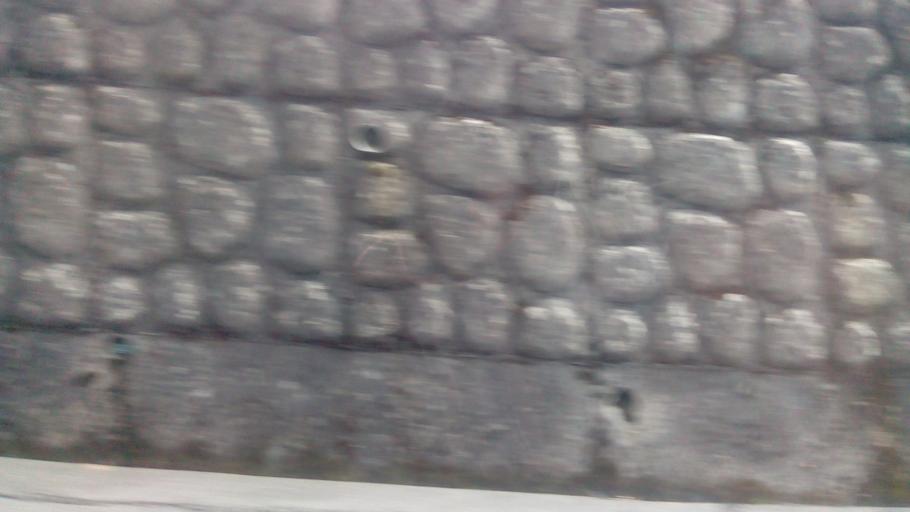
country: TW
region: Taiwan
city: Daxi
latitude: 24.4637
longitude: 121.3964
